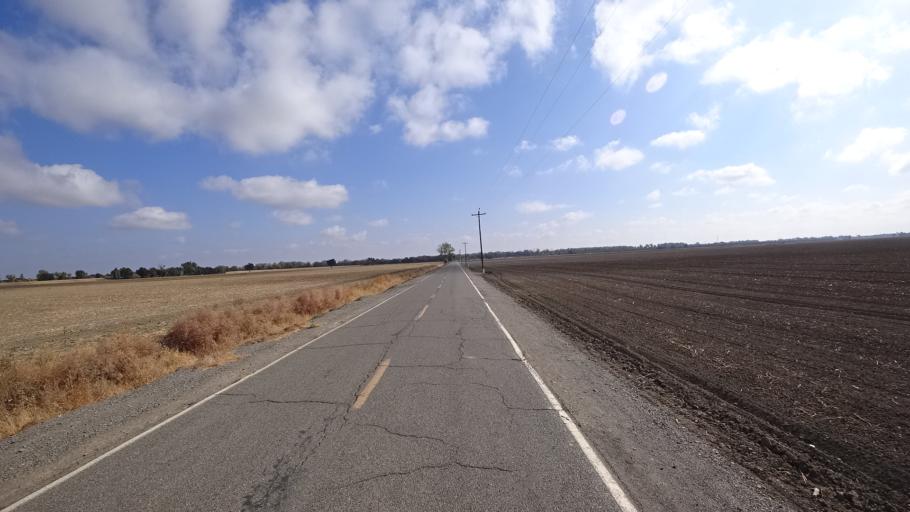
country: US
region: California
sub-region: Yolo County
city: Woodland
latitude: 38.7959
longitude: -121.7141
